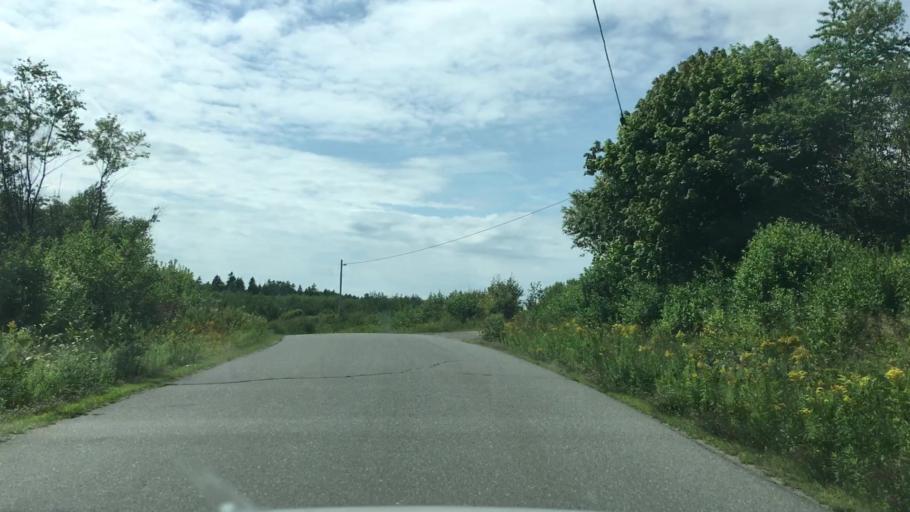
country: US
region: Maine
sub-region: Washington County
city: Eastport
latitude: 44.9069
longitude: -67.0028
